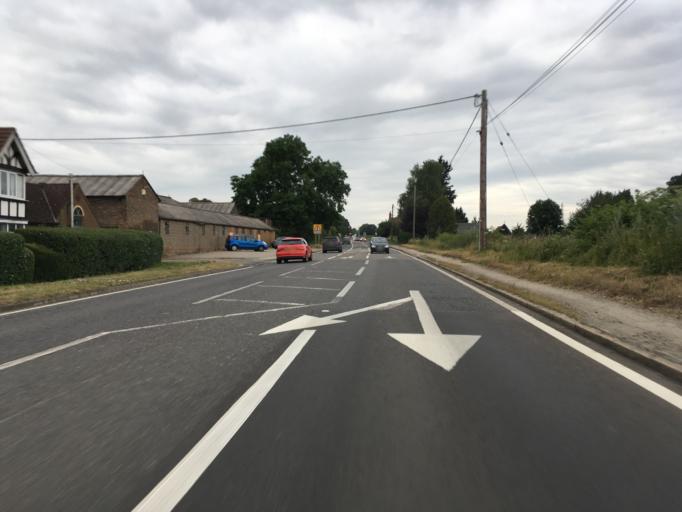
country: GB
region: England
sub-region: Central Bedfordshire
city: Kensworth
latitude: 51.8649
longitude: -0.4867
